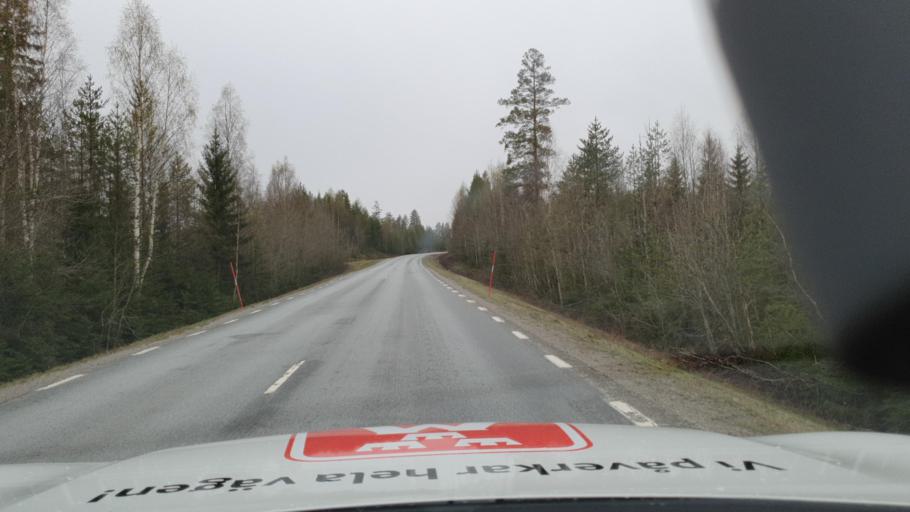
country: SE
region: Vaesterbotten
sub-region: Vannas Kommun
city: Vaennaes
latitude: 63.7824
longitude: 19.7393
